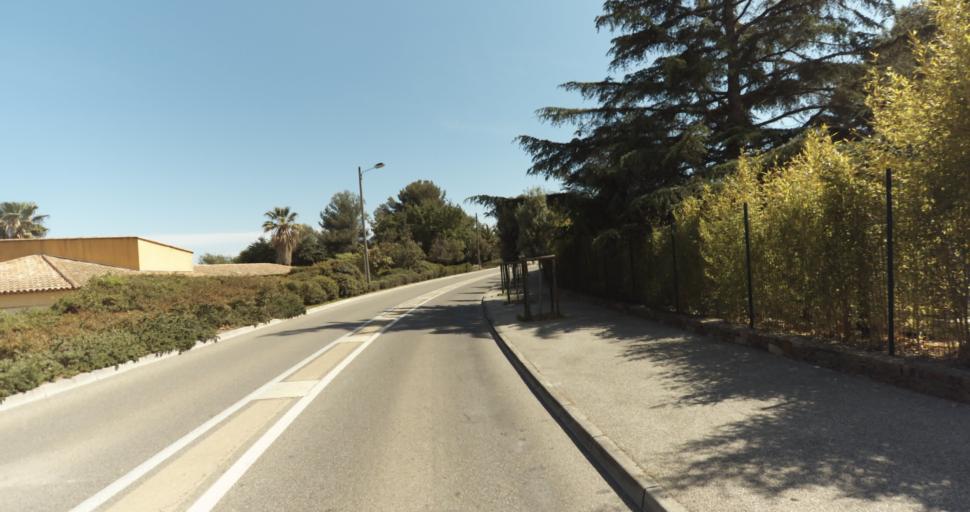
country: FR
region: Provence-Alpes-Cote d'Azur
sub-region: Departement du Var
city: Hyeres
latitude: 43.0883
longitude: 6.1220
